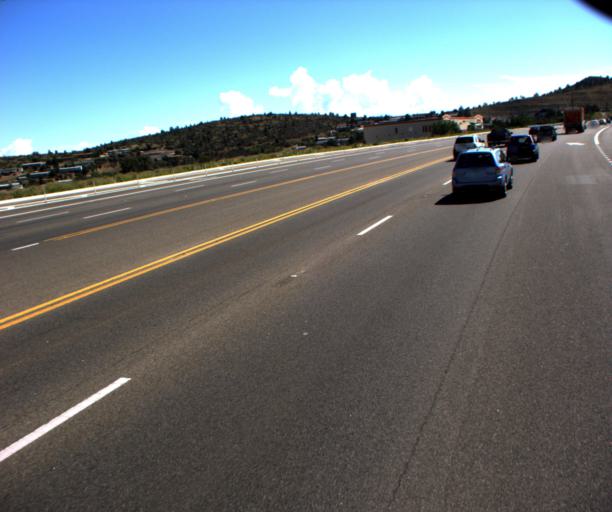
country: US
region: Arizona
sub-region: Yavapai County
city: Prescott
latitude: 34.5519
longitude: -112.4313
